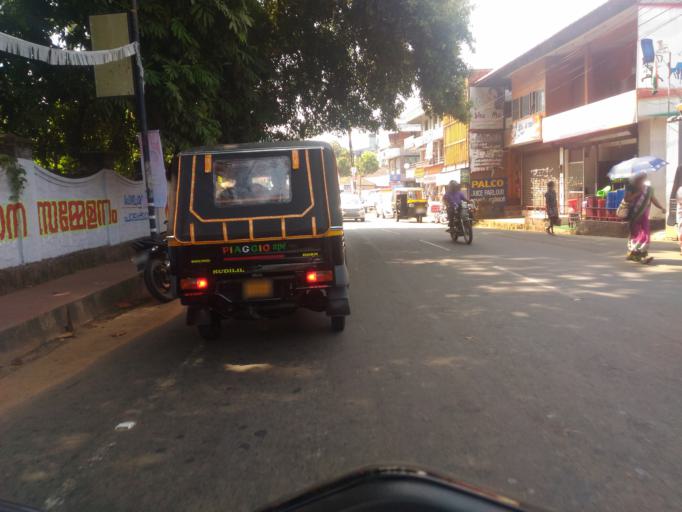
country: IN
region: Kerala
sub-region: Ernakulam
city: Muvattupula
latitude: 9.8966
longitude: 76.7090
